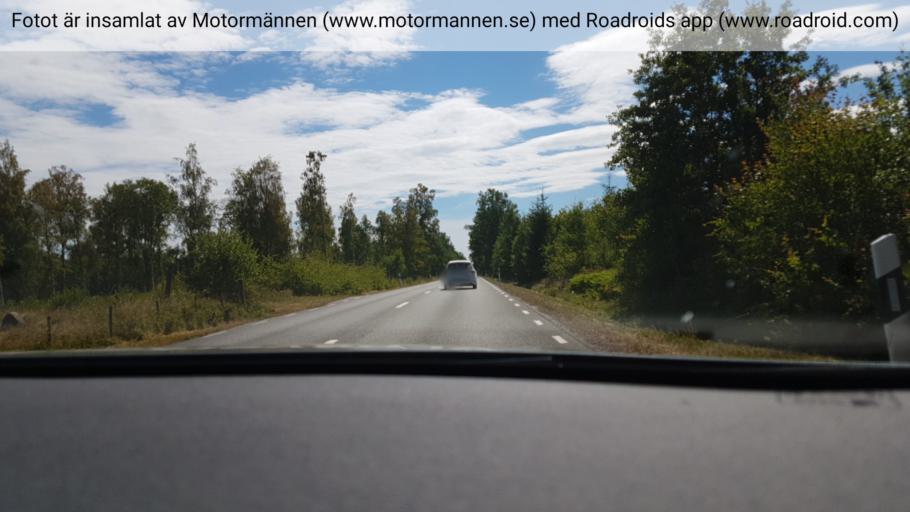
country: SE
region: Joenkoeping
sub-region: Jonkopings Kommun
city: Asa
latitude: 57.9897
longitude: 14.7545
